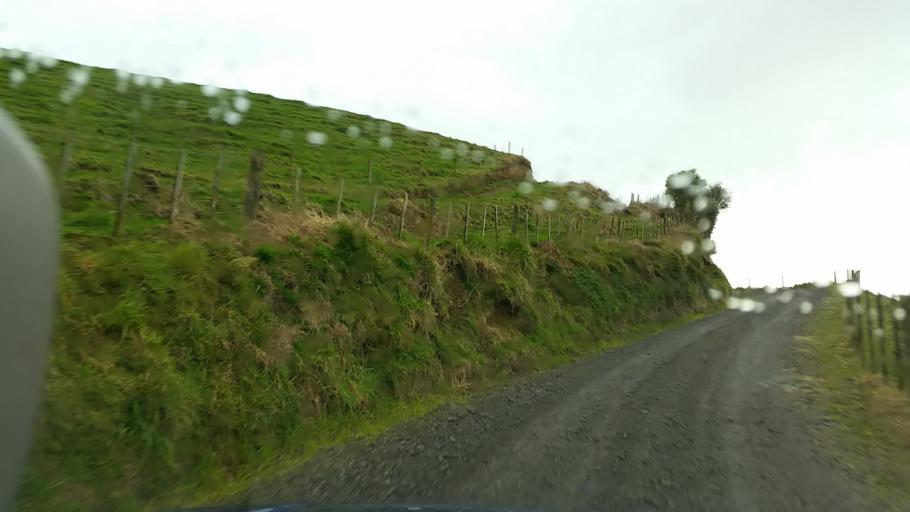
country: NZ
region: Taranaki
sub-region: South Taranaki District
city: Eltham
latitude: -39.2808
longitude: 174.3369
